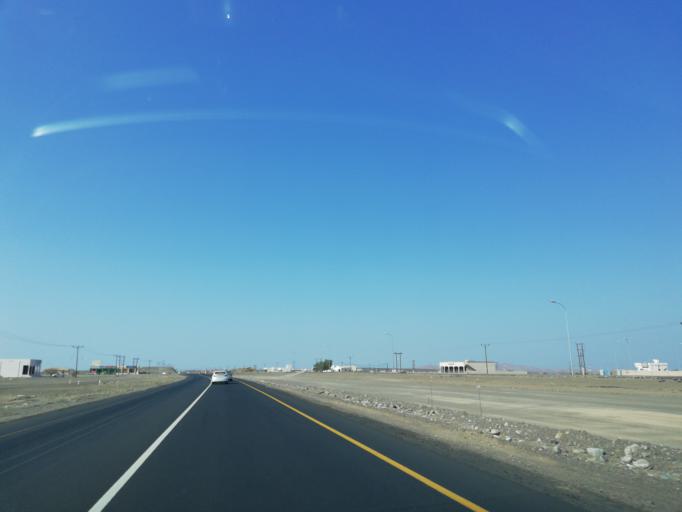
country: OM
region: Ash Sharqiyah
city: Ibra'
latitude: 22.7057
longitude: 58.1420
